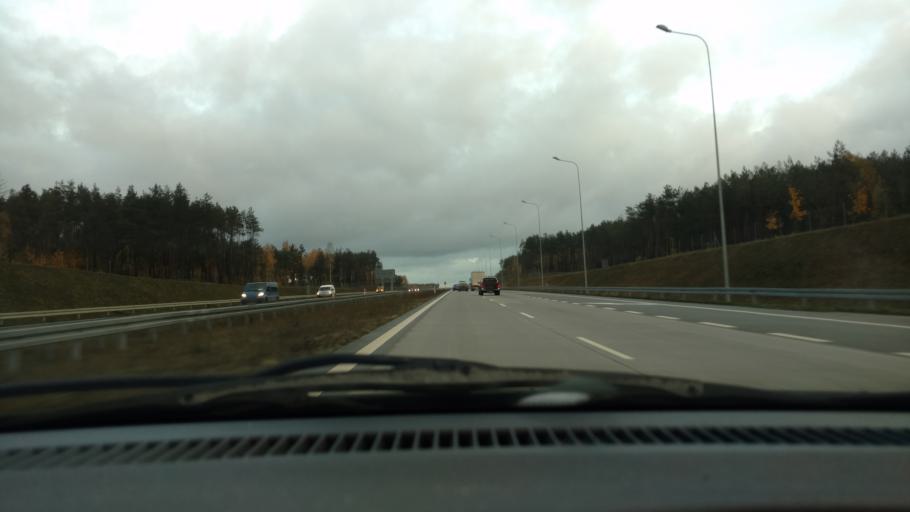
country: PL
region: Lodz Voivodeship
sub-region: Powiat lodzki wschodni
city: Tuszyn
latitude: 51.6520
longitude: 19.5780
